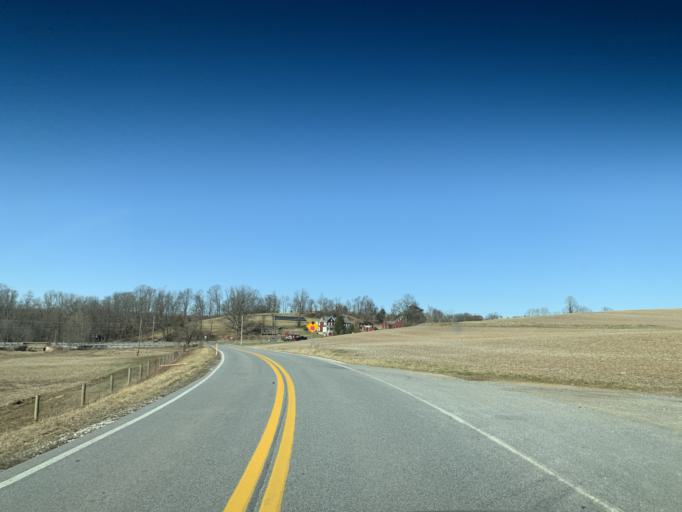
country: US
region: Maryland
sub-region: Carroll County
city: Manchester
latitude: 39.6528
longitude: -76.9565
